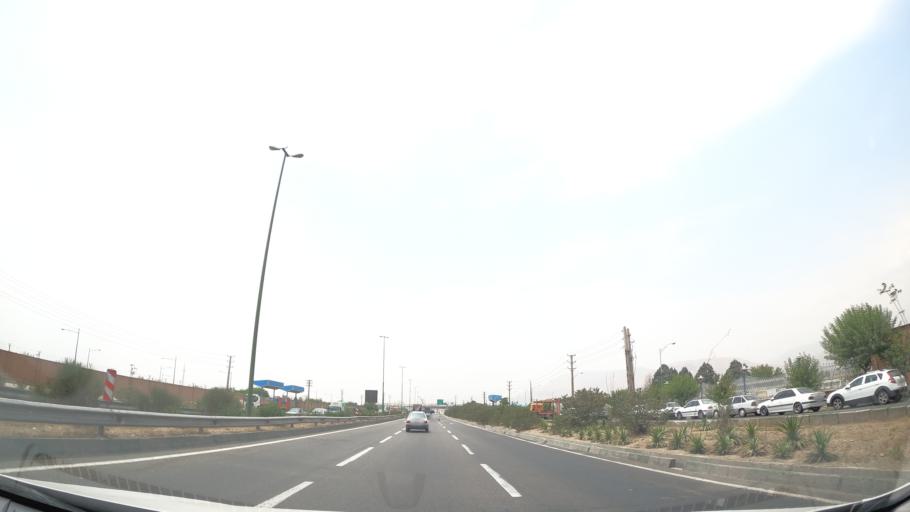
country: IR
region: Tehran
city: Shahr-e Qods
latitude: 35.7010
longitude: 51.1898
